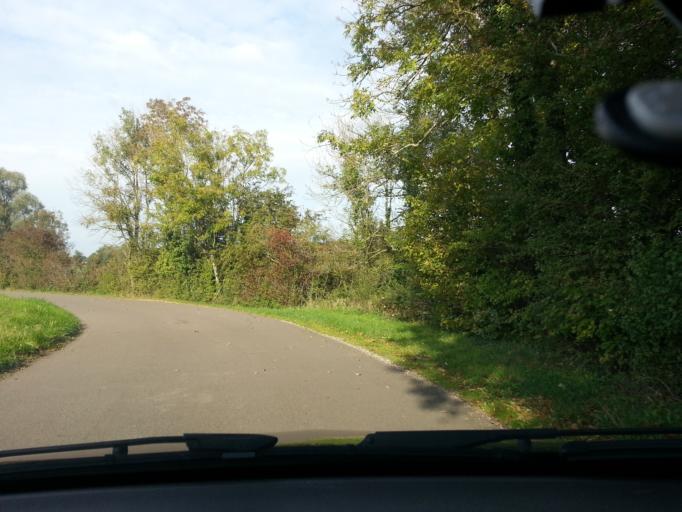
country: FR
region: Bourgogne
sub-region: Departement de Saone-et-Loire
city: Dracy-le-Fort
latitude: 46.7853
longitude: 4.7812
